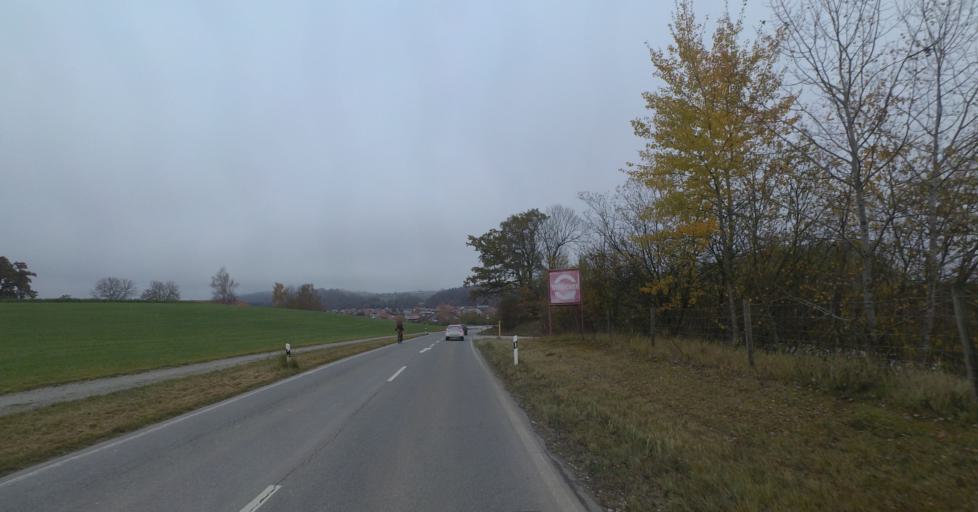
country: DE
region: Bavaria
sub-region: Upper Bavaria
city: Trostberg an der Alz
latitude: 47.9843
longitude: 12.5348
